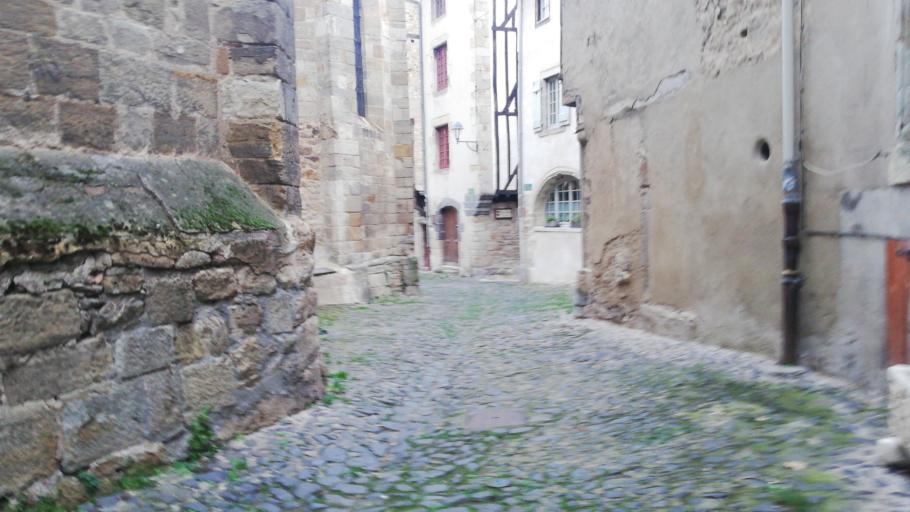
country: FR
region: Auvergne
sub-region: Departement du Puy-de-Dome
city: Billom
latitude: 45.7222
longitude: 3.3377
